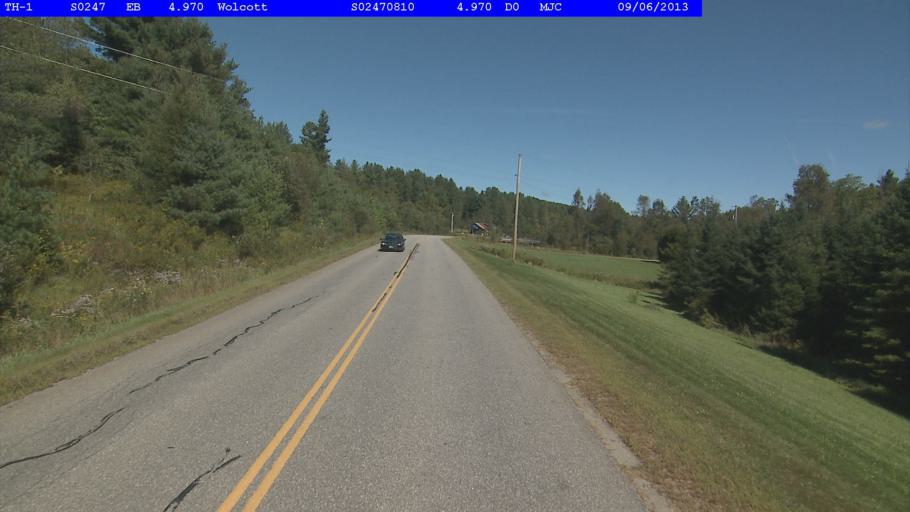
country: US
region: Vermont
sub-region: Caledonia County
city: Hardwick
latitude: 44.6166
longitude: -72.4460
